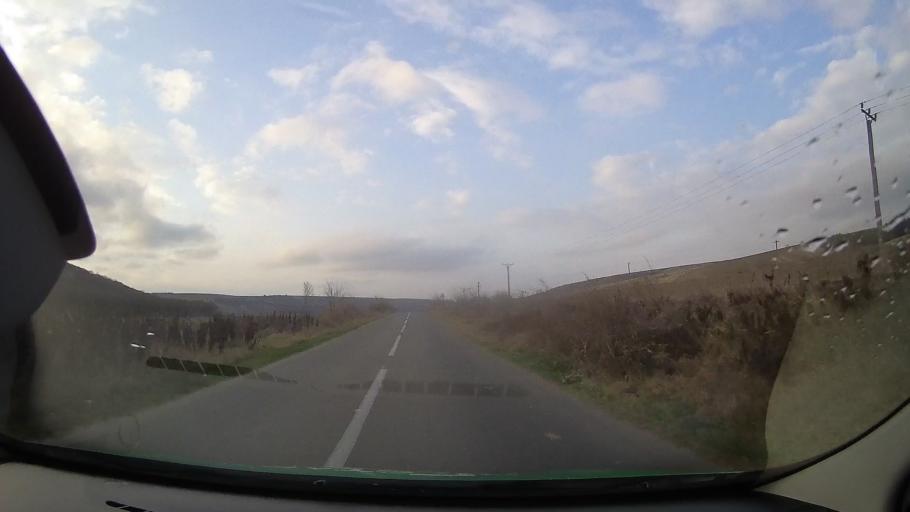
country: RO
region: Constanta
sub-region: Comuna Dobromir
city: Dobromir
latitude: 44.0332
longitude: 27.8553
